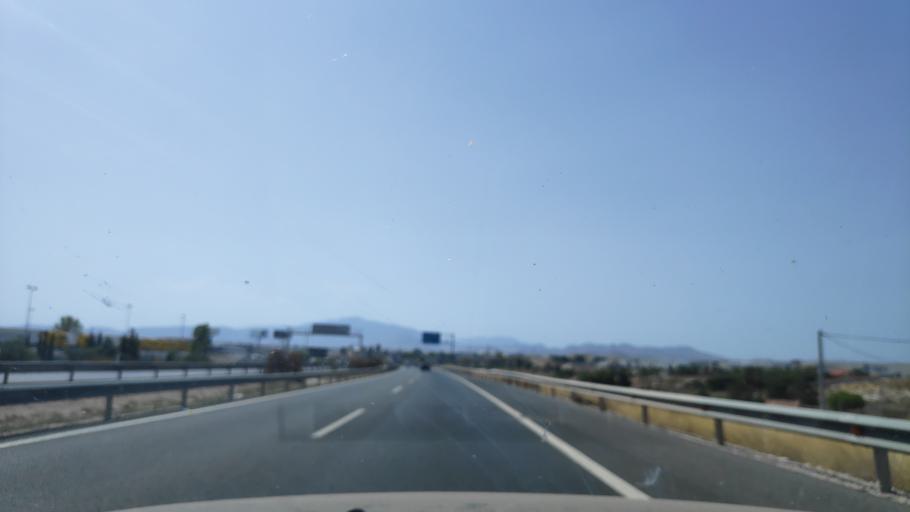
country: ES
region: Murcia
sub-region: Murcia
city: Molina de Segura
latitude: 38.0788
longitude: -1.2119
